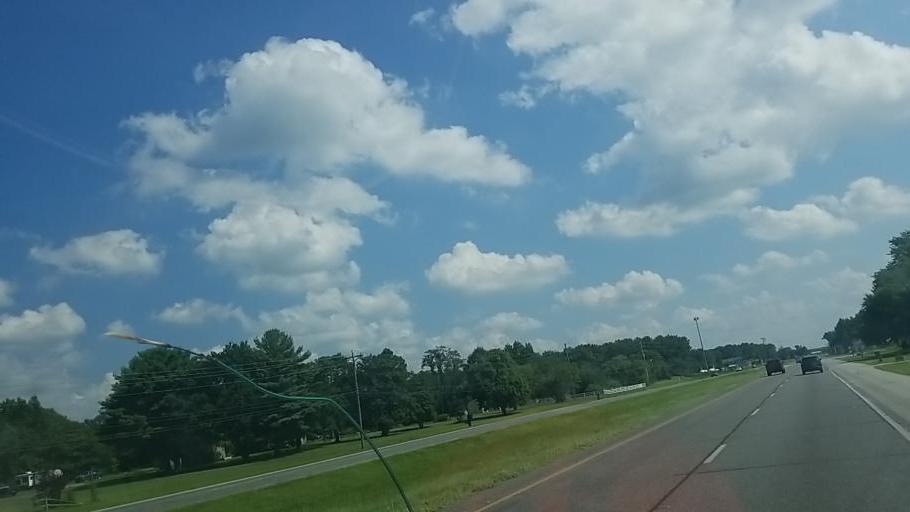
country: US
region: Delaware
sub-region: Sussex County
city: Georgetown
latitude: 38.7134
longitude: -75.4063
